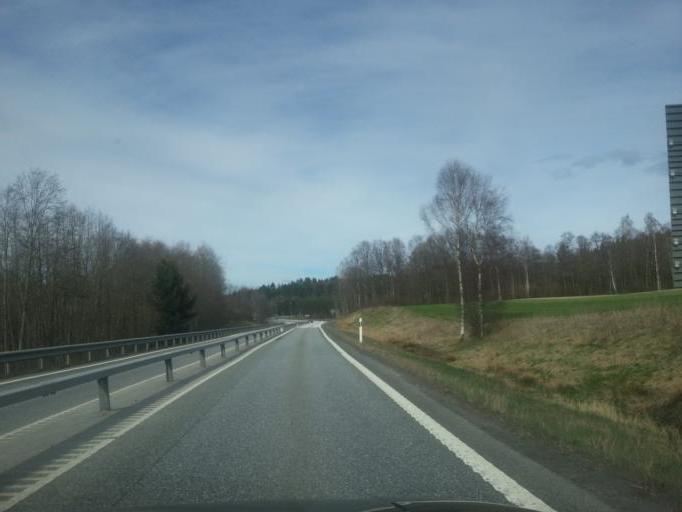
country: SE
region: Joenkoeping
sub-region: Jonkopings Kommun
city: Bankeryd
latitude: 57.8613
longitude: 14.1036
